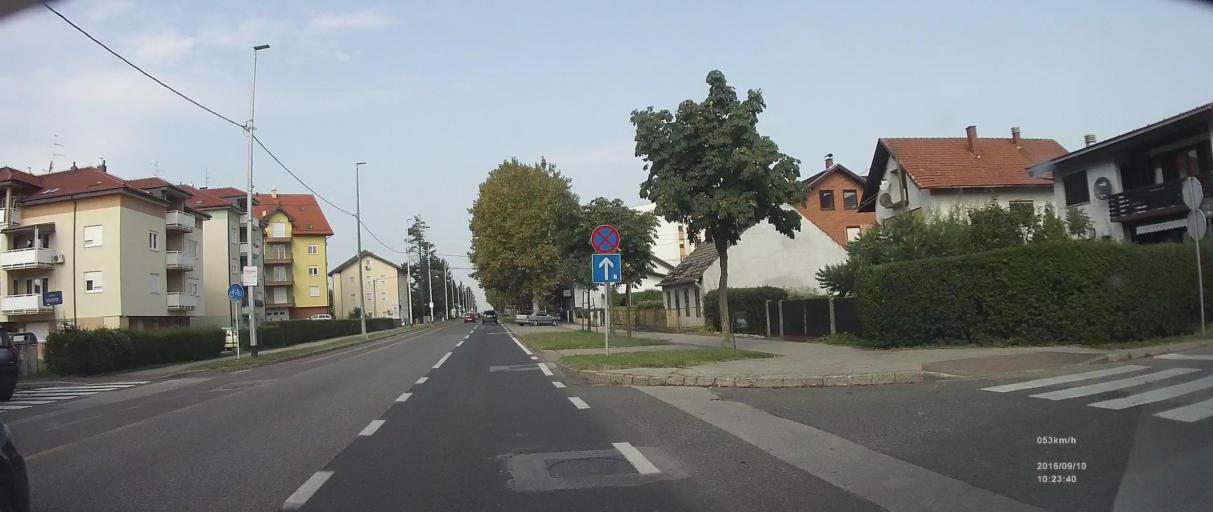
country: HR
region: Zagrebacka
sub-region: Grad Velika Gorica
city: Velika Gorica
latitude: 45.7185
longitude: 16.0627
